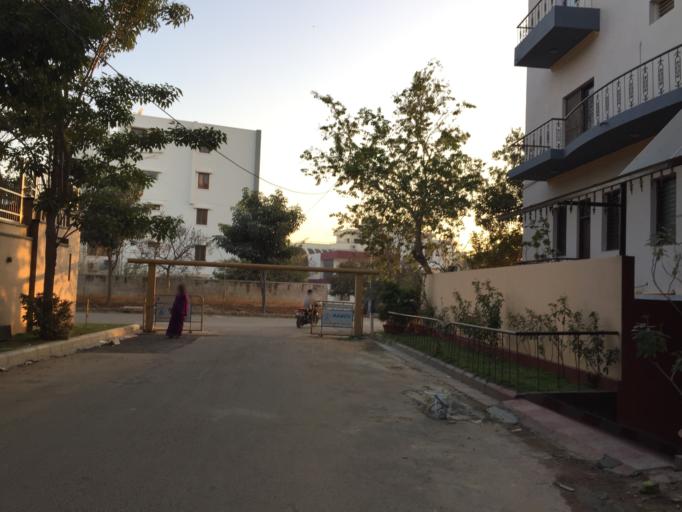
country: IN
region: Karnataka
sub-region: Bangalore Urban
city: Yelahanka
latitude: 13.0555
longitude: 77.6249
